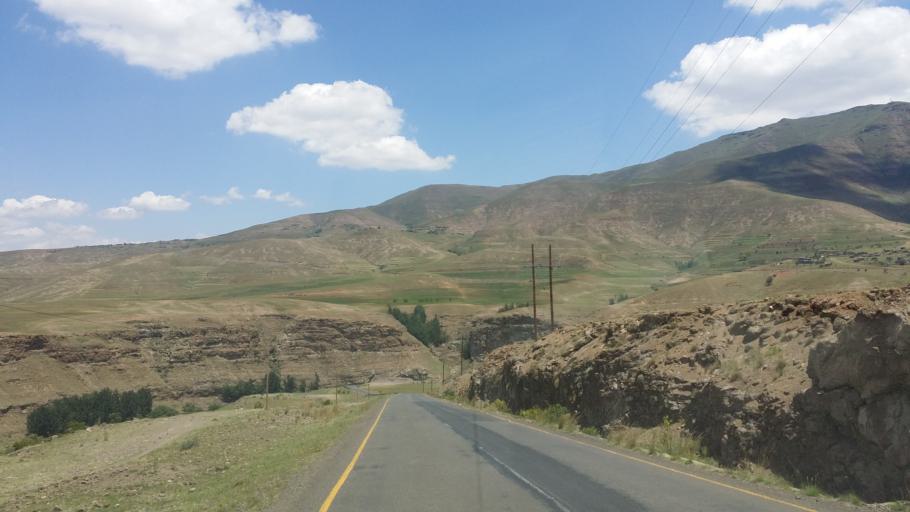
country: LS
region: Mokhotlong
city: Mokhotlong
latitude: -29.2937
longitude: 28.9940
